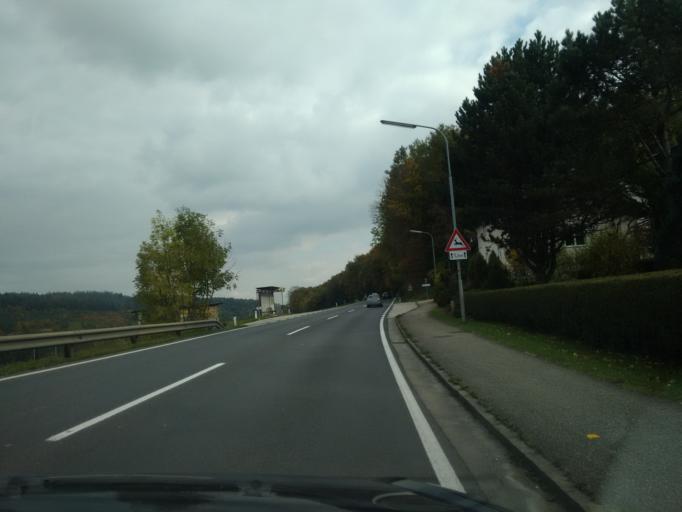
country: AT
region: Upper Austria
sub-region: Politischer Bezirk Vocklabruck
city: Attnang-Puchheim
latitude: 48.0066
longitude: 13.6855
